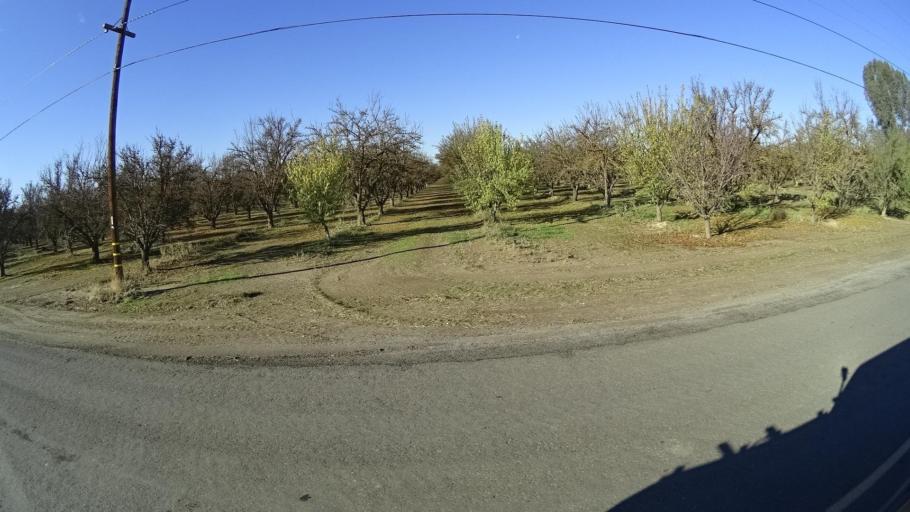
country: US
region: California
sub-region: Kern County
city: Delano
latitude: 35.7550
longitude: -119.3119
